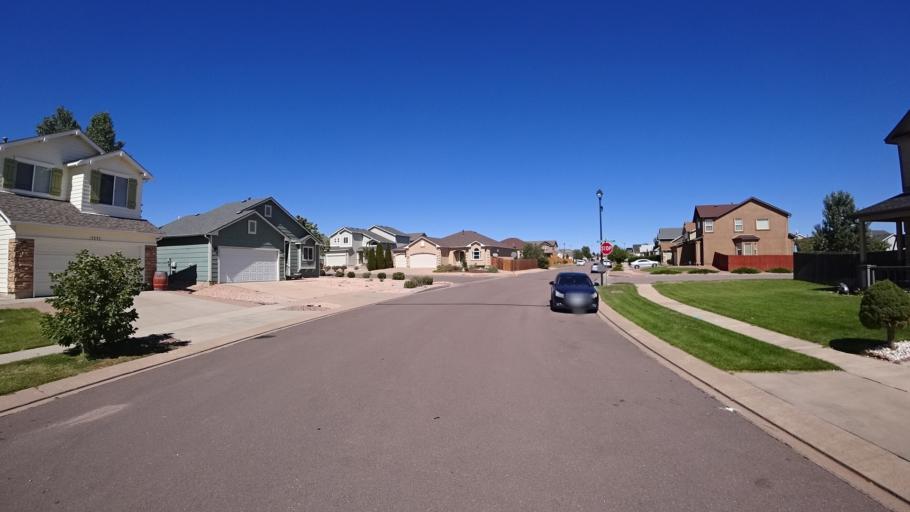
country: US
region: Colorado
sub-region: El Paso County
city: Security-Widefield
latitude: 38.7828
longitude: -104.7283
